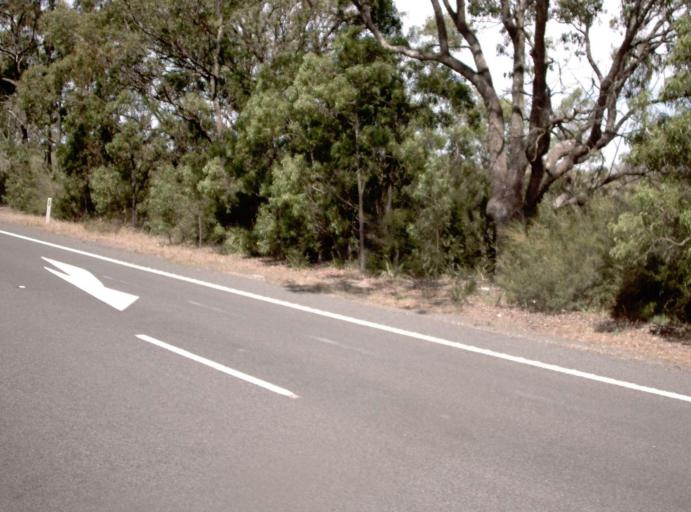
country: AU
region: Victoria
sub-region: Wellington
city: Sale
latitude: -37.9399
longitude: 147.1483
